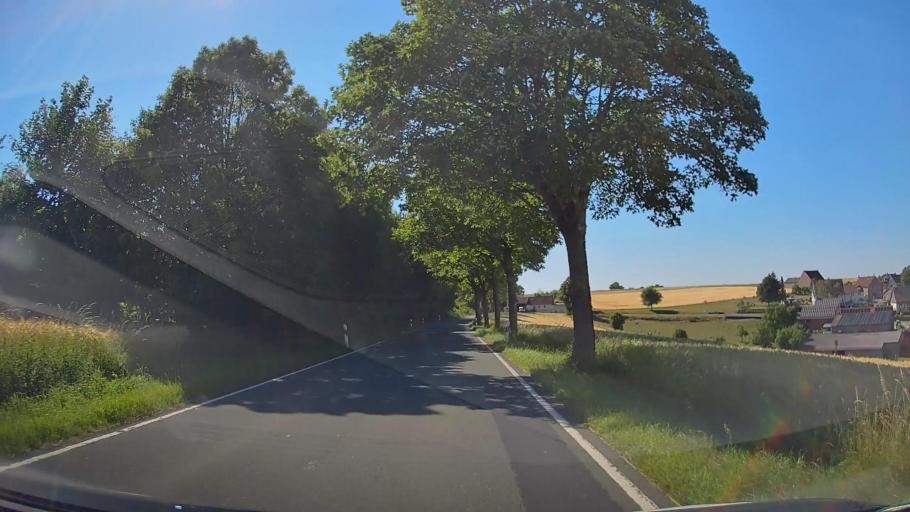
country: DE
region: Lower Saxony
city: Vahlbruch
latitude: 51.9558
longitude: 9.3014
